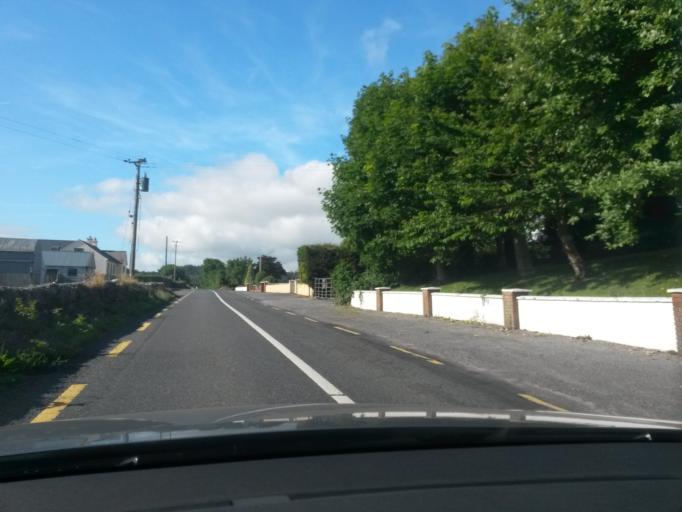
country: IE
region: Connaught
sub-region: Sligo
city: Sligo
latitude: 54.2332
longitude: -8.4720
